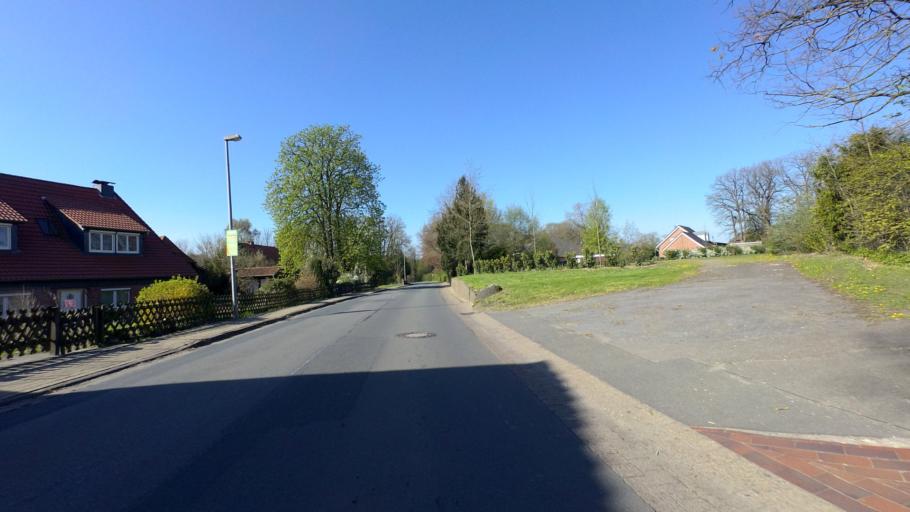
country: DE
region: Lower Saxony
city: Stockse
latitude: 52.6430
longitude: 9.3442
